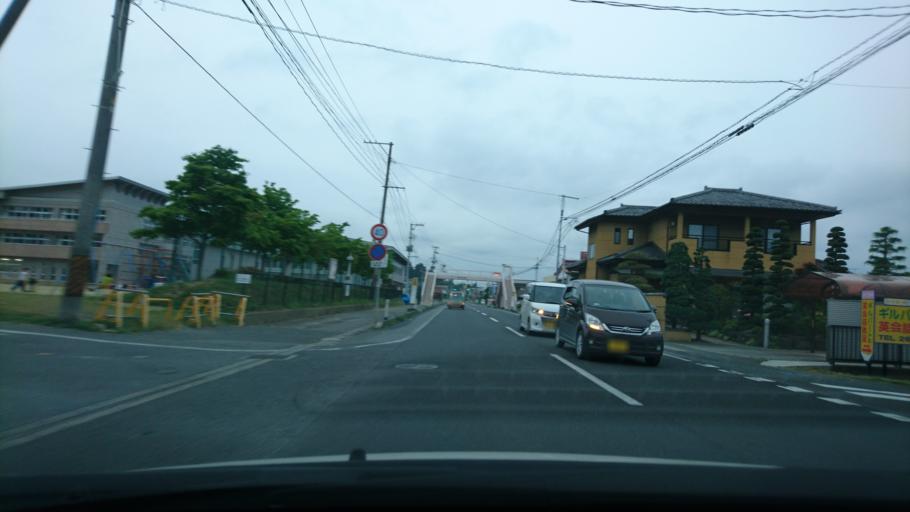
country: JP
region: Iwate
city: Ichinoseki
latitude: 38.9149
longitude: 141.1316
